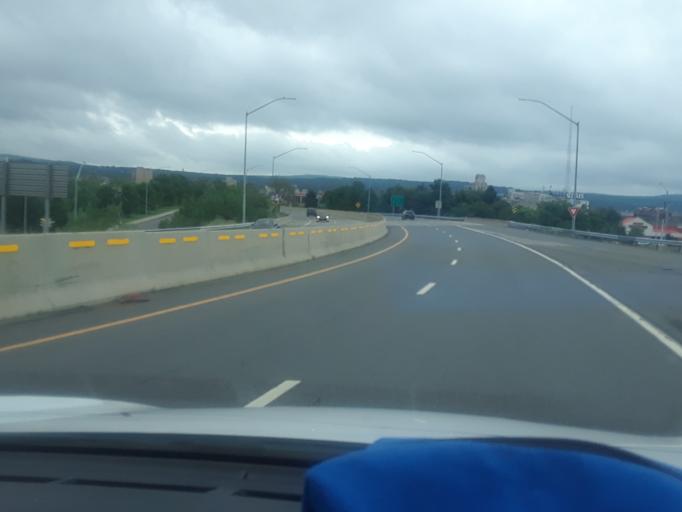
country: US
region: Pennsylvania
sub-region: Lackawanna County
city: Scranton
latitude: 41.4167
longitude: -75.6703
